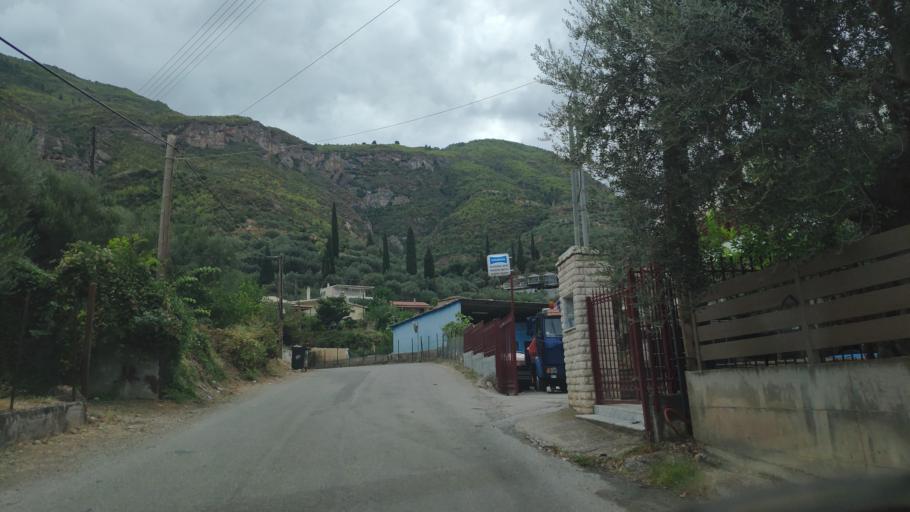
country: GR
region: West Greece
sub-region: Nomos Achaias
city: Temeni
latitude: 38.1793
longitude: 22.1445
